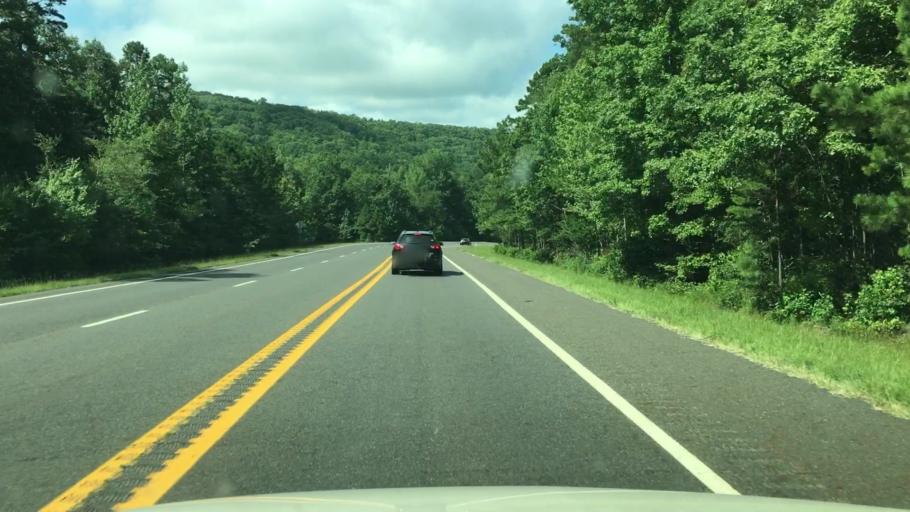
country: US
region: Arkansas
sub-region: Garland County
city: Lake Hamilton
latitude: 34.3641
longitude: -93.1627
